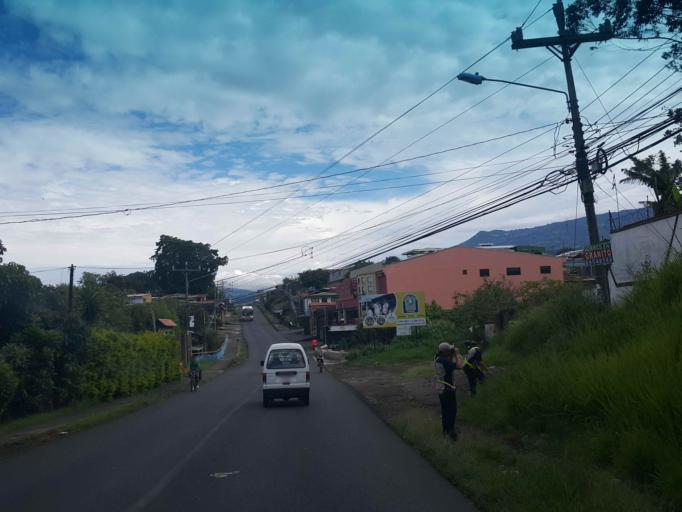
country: CR
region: Heredia
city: Heredia
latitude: 10.0078
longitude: -84.1176
